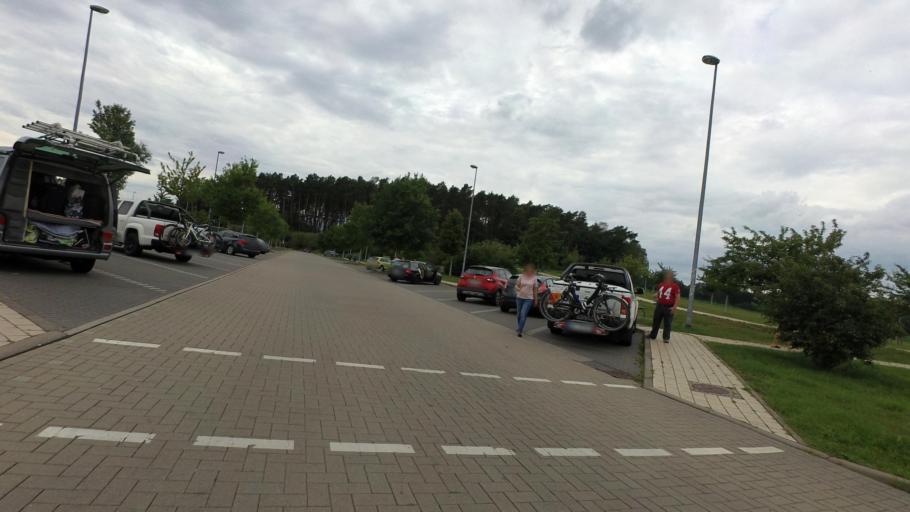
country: DE
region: Brandenburg
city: Joachimsthal
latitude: 52.8827
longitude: 13.7005
